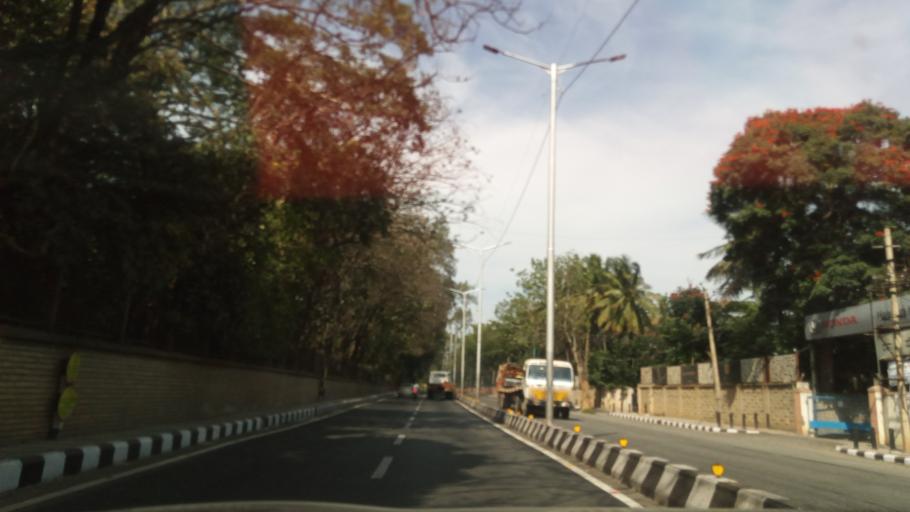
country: IN
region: Karnataka
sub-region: Bangalore Urban
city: Bangalore
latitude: 13.0330
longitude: 77.5408
